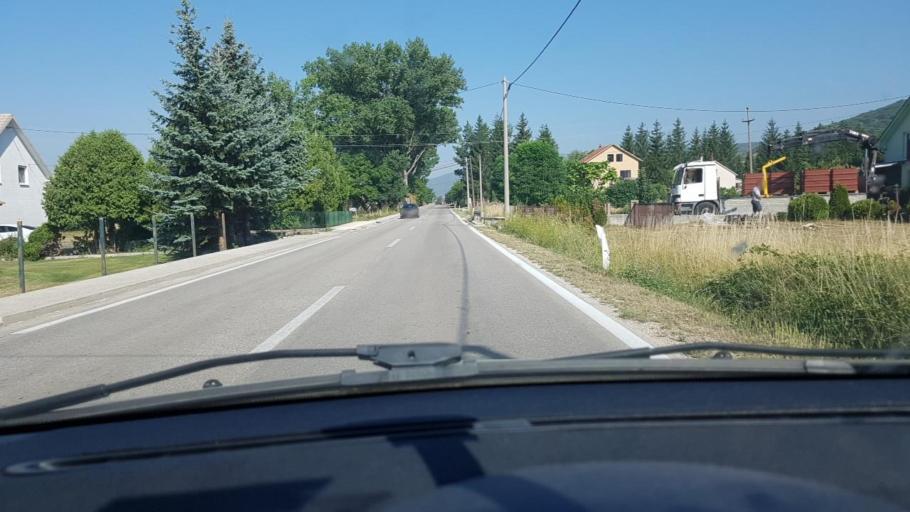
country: BA
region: Federation of Bosnia and Herzegovina
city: Livno
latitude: 43.8370
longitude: 16.9797
